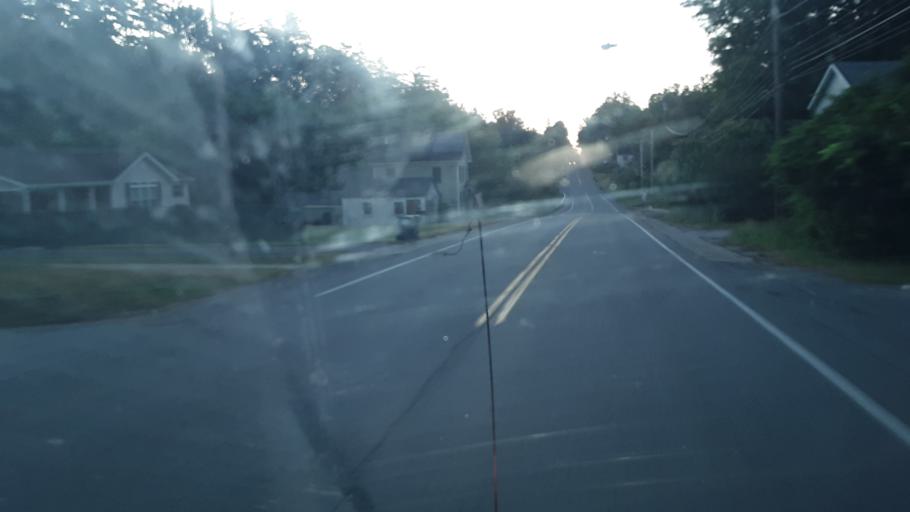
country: US
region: New York
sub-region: Saratoga County
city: Ballston Spa
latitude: 43.0001
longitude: -73.8591
